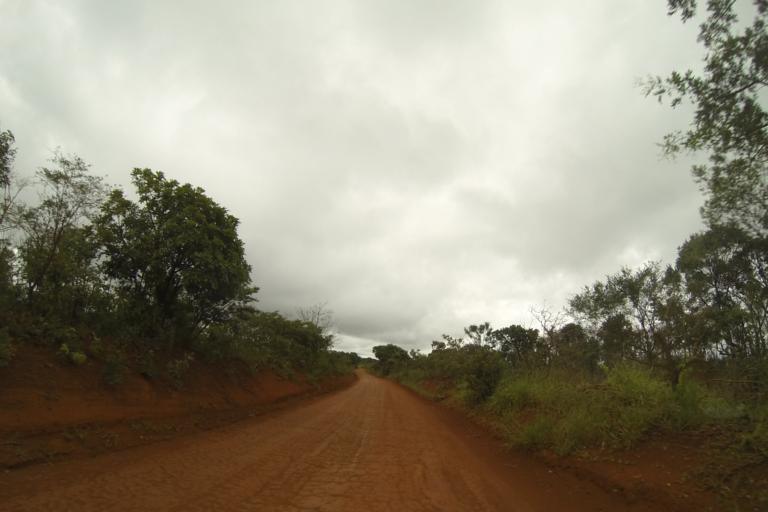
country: BR
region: Minas Gerais
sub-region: Campos Altos
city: Campos Altos
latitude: -19.8271
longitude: -46.3223
